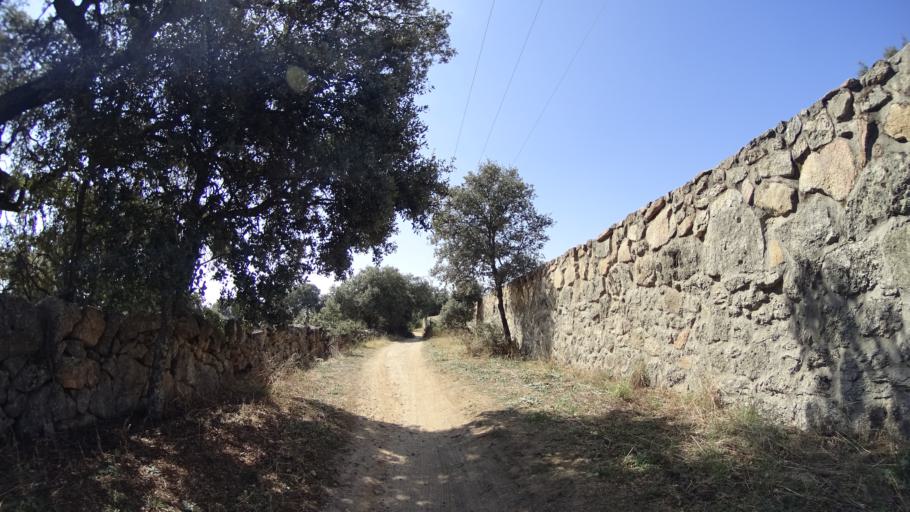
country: ES
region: Madrid
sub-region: Provincia de Madrid
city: Colmenarejo
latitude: 40.5707
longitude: -4.0258
